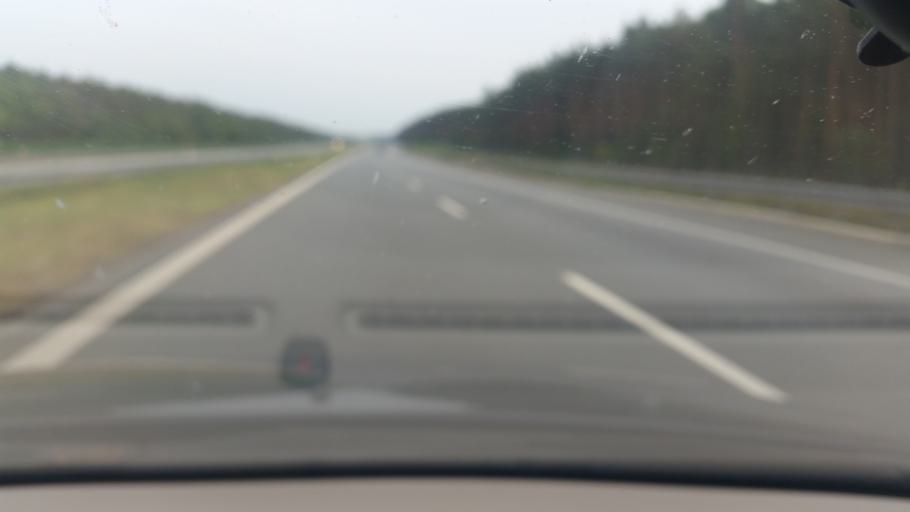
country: PL
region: Kujawsko-Pomorskie
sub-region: Powiat aleksandrowski
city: Aleksandrow Kujawski
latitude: 52.8883
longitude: 18.7325
